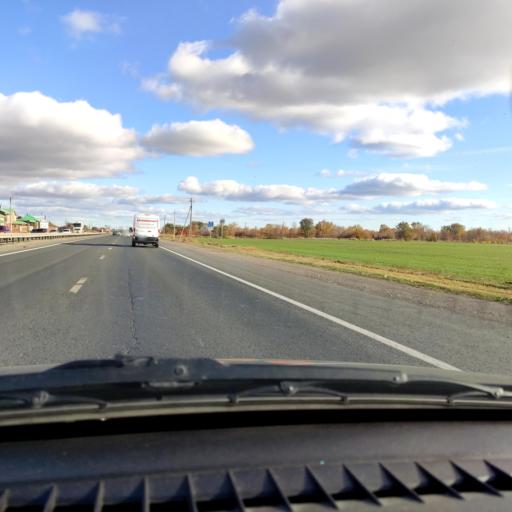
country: RU
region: Samara
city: Tol'yatti
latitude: 53.5707
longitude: 49.4719
